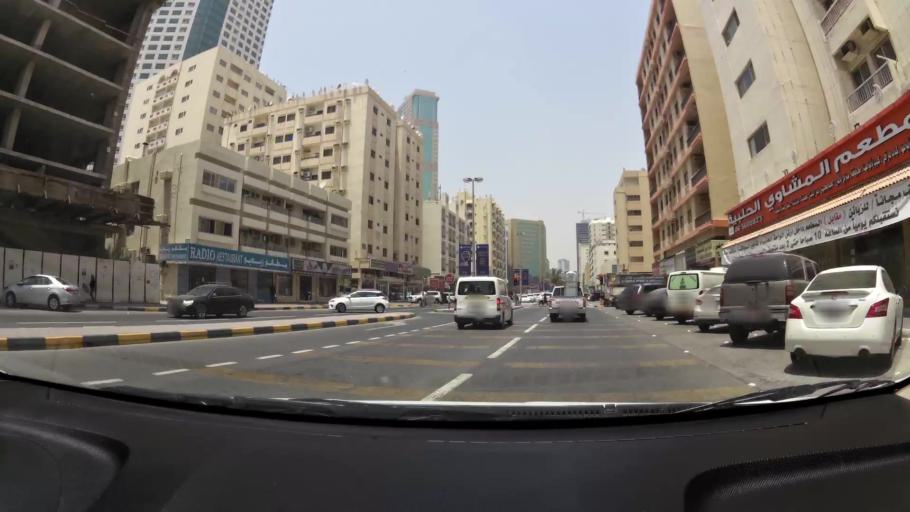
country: AE
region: Ash Shariqah
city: Sharjah
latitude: 25.3190
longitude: 55.3844
